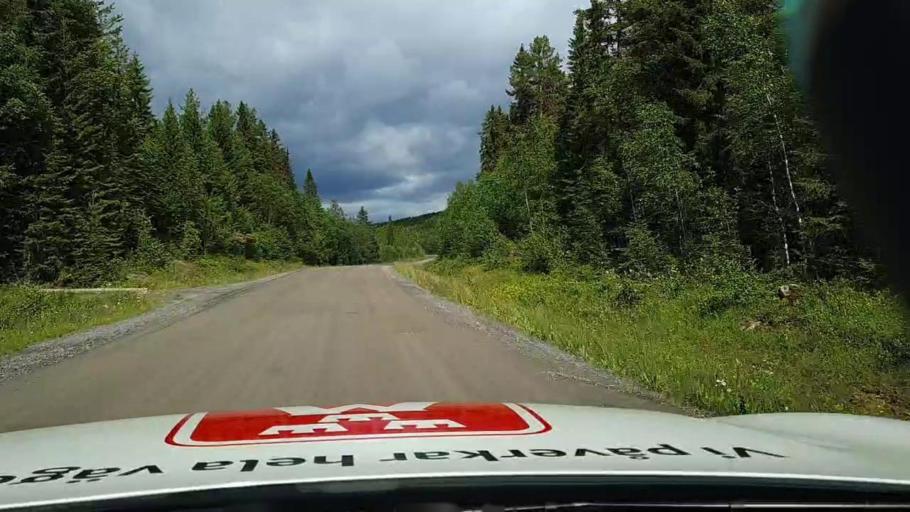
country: SE
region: Vaesternorrland
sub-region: Solleftea Kommun
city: As
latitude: 63.4726
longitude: 16.2840
